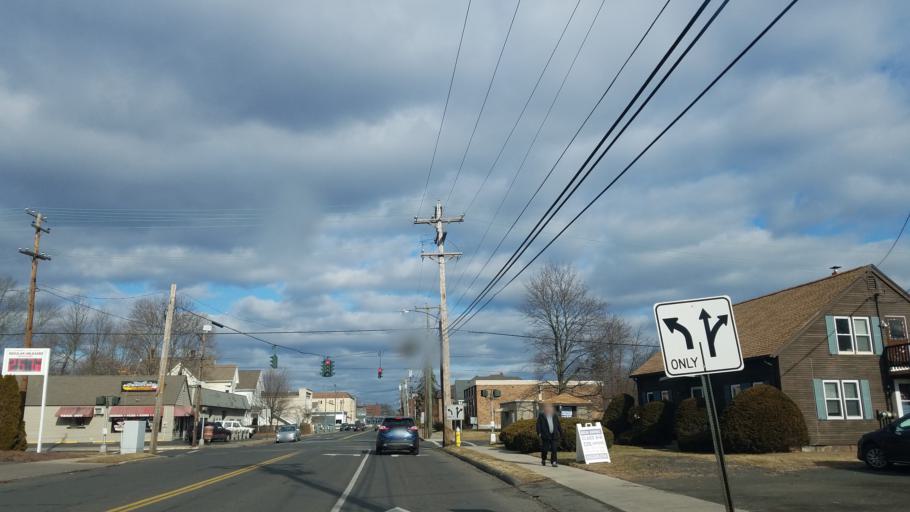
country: US
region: Connecticut
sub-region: Hartford County
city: Plainville
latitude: 41.6674
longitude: -72.8672
